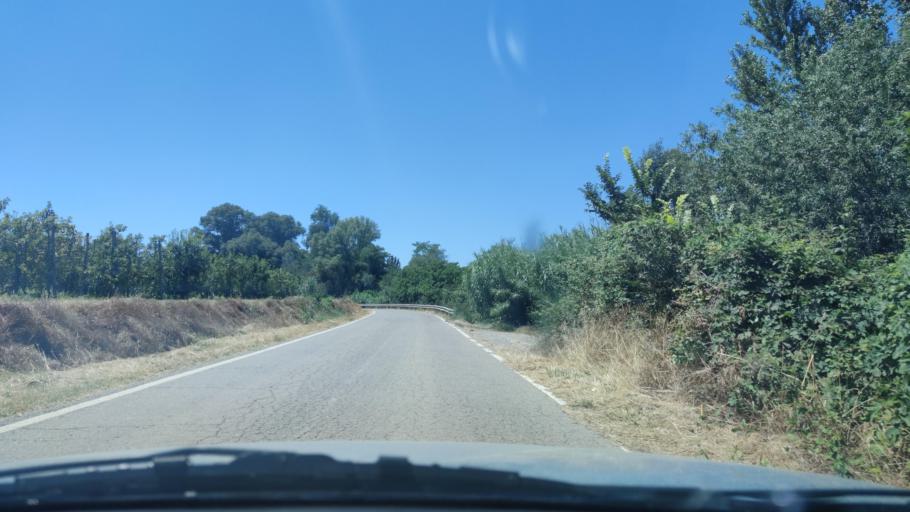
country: ES
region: Catalonia
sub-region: Provincia de Lleida
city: Alcoletge
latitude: 41.6559
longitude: 0.6740
